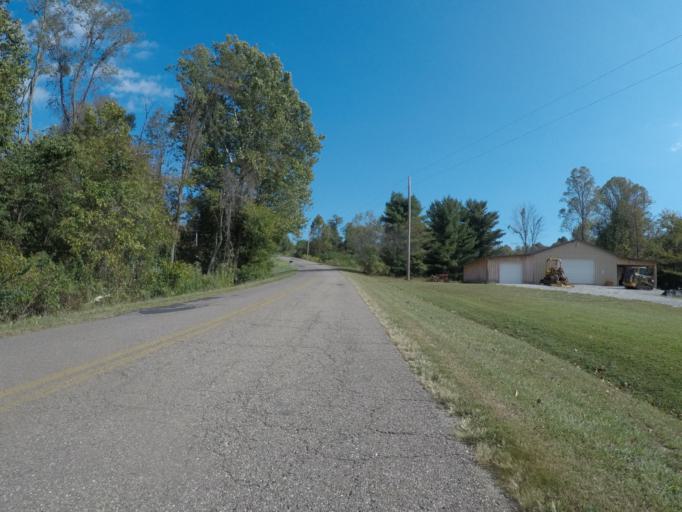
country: US
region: West Virginia
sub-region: Cabell County
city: Lesage
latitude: 38.5975
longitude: -82.4146
